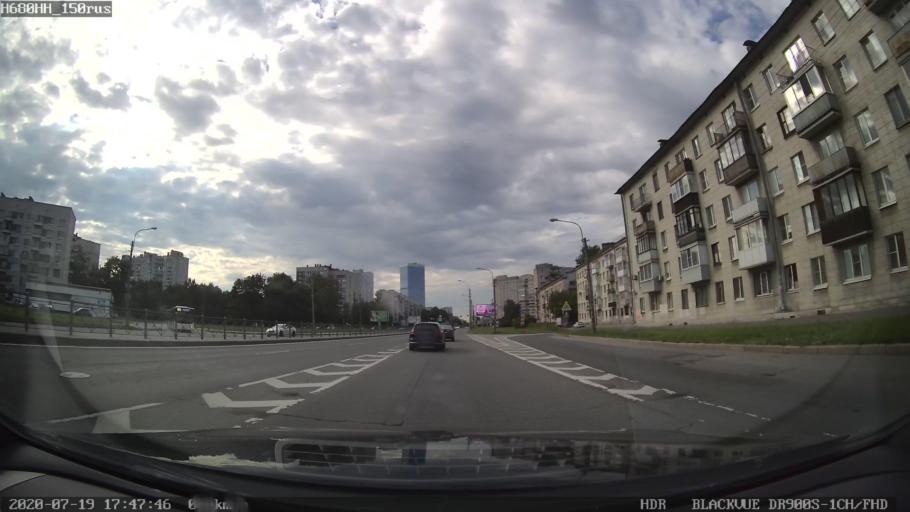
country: RU
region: St.-Petersburg
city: Kupchino
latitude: 59.8439
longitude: 30.3131
